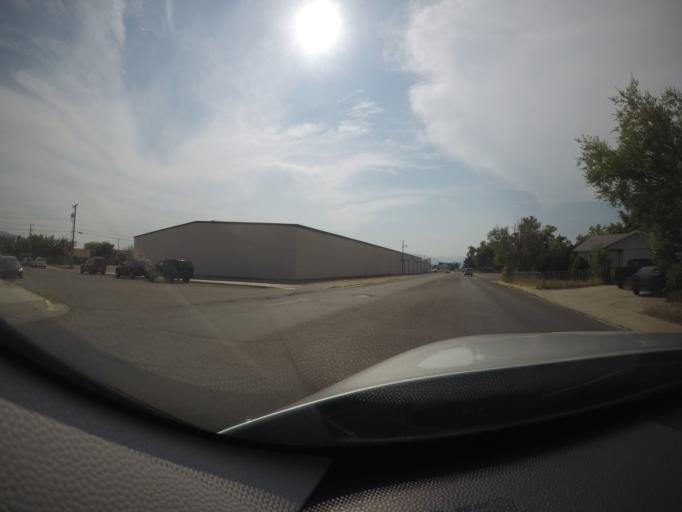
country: US
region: Montana
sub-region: Missoula County
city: Missoula
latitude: 46.8560
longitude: -114.0094
